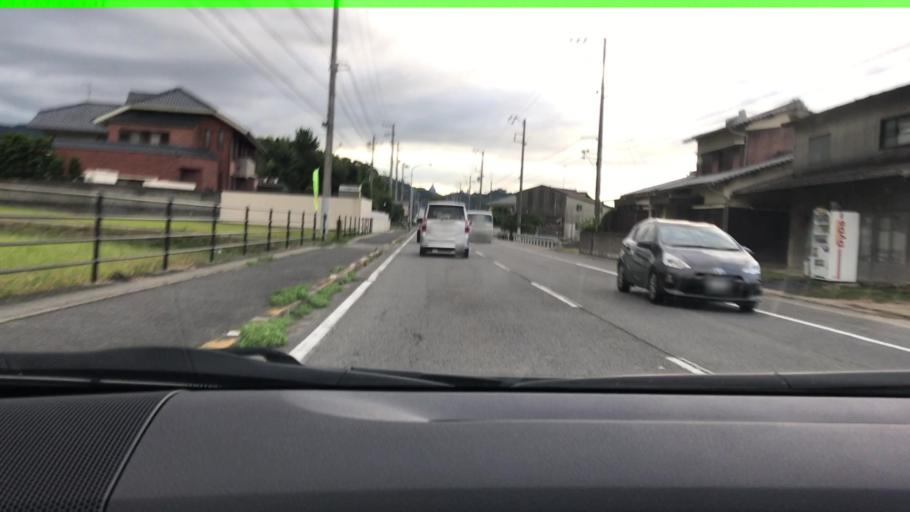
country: JP
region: Ehime
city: Hojo
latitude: 34.0655
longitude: 132.9333
